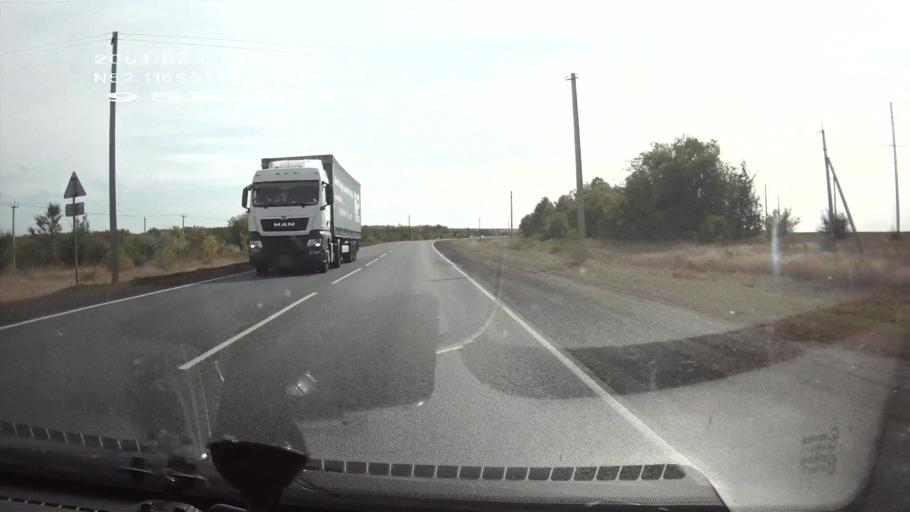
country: RU
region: Saratov
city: Balakovo
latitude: 52.1161
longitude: 47.7510
